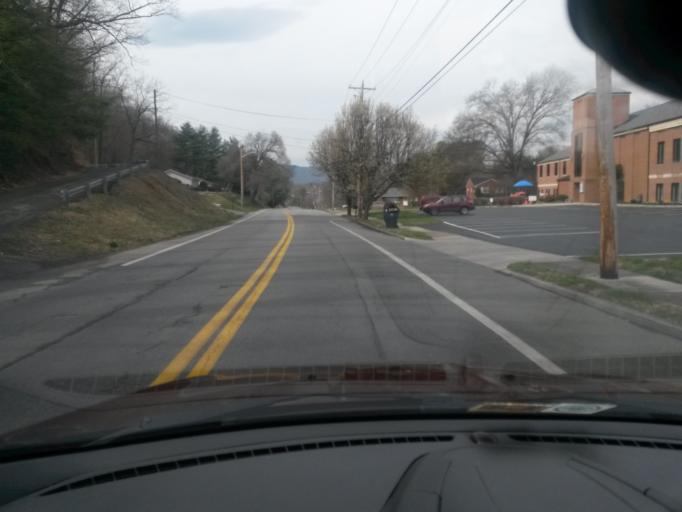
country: US
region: Virginia
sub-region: Roanoke County
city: Cave Spring
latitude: 37.2541
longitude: -79.9920
